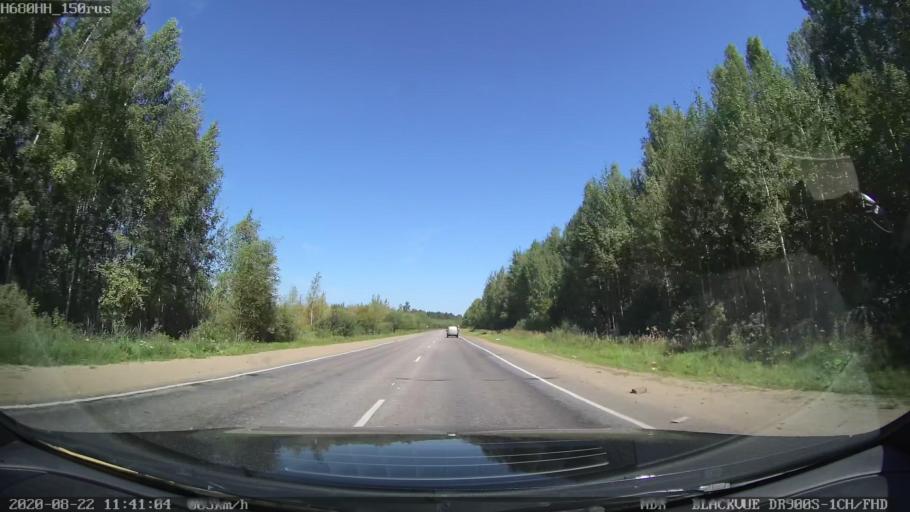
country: RU
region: Tverskaya
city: Sakharovo
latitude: 56.9847
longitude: 36.0237
